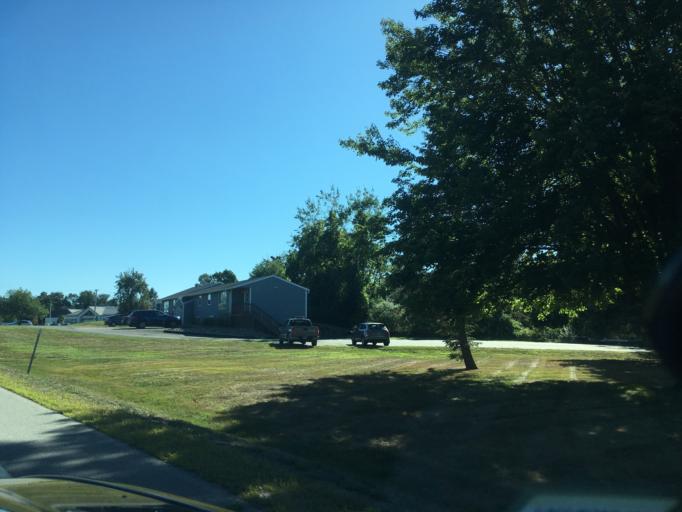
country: US
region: New Hampshire
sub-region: Rockingham County
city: Exeter
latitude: 43.0130
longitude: -70.9176
